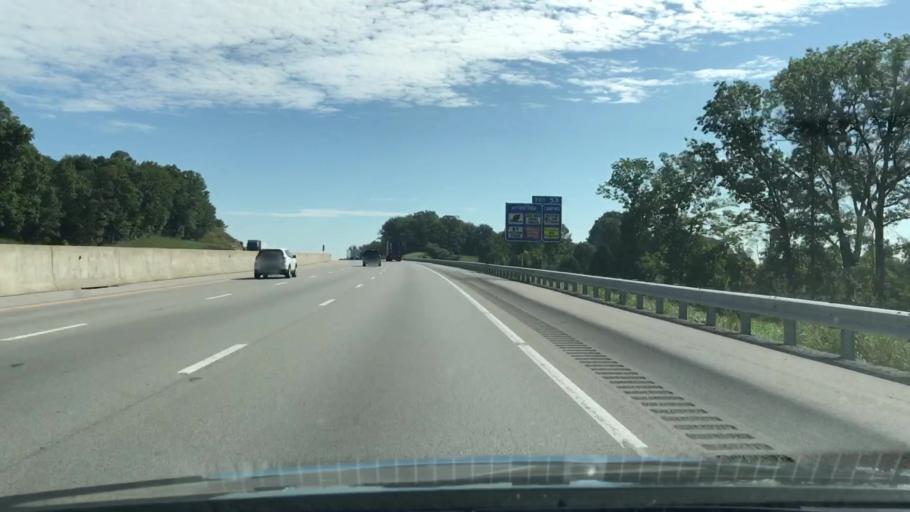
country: US
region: Kentucky
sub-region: Barren County
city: Cave City
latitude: 37.1214
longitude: -86.0014
